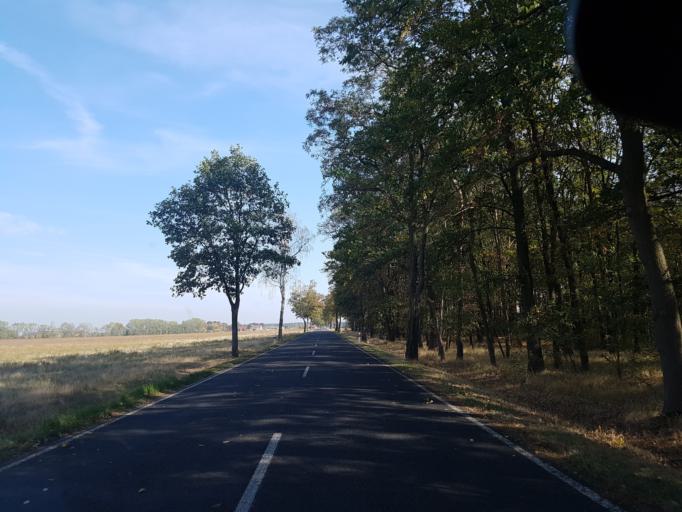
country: DE
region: Brandenburg
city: Lebusa
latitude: 51.8262
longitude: 13.3756
